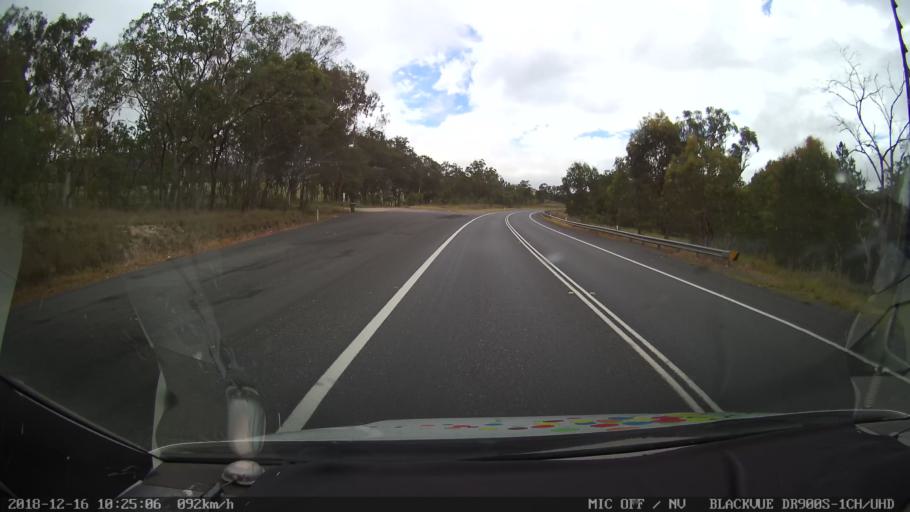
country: AU
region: New South Wales
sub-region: Tenterfield Municipality
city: Carrolls Creek
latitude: -29.1631
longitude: 152.0009
